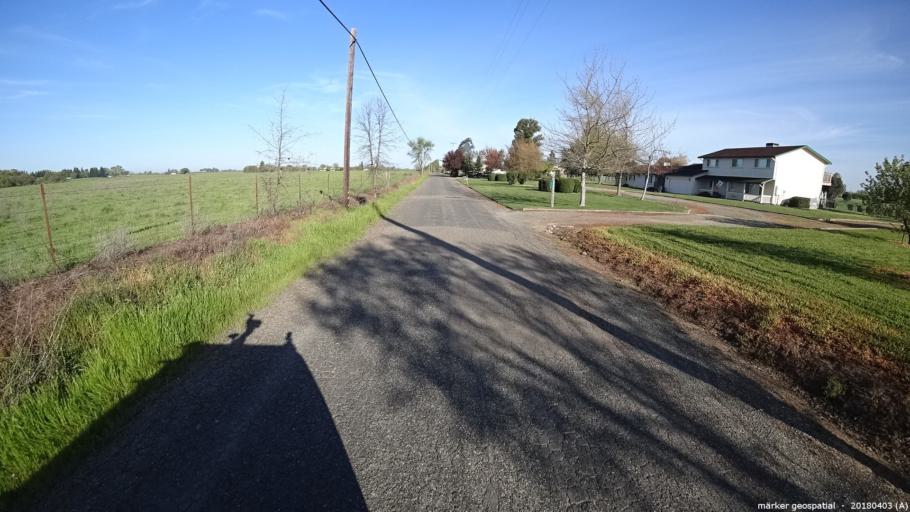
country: US
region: California
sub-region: Sacramento County
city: Wilton
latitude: 38.4428
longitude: -121.1987
